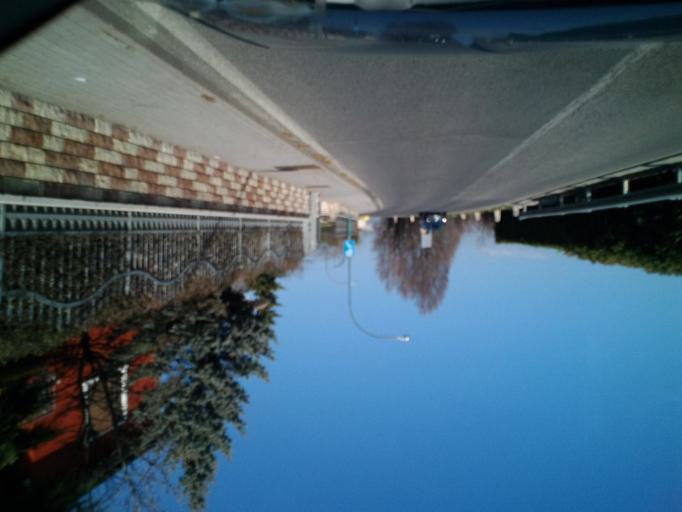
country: IT
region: Veneto
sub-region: Provincia di Verona
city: Cerro Veronese
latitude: 45.5732
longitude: 11.0398
